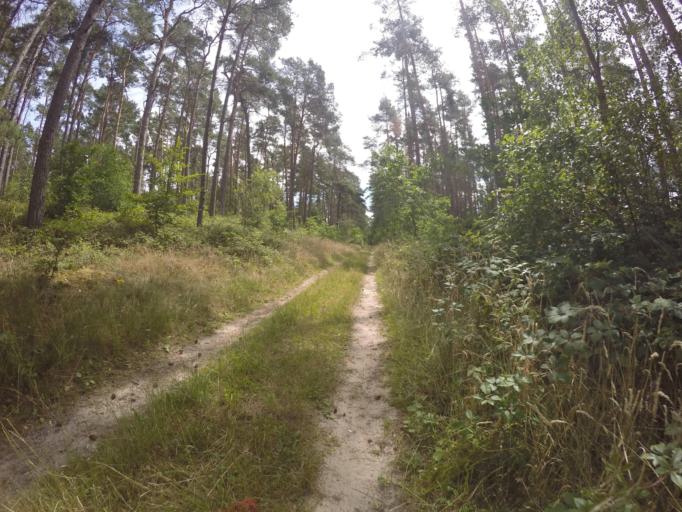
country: DE
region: Lower Saxony
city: Thomasburg
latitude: 53.2525
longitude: 10.6628
